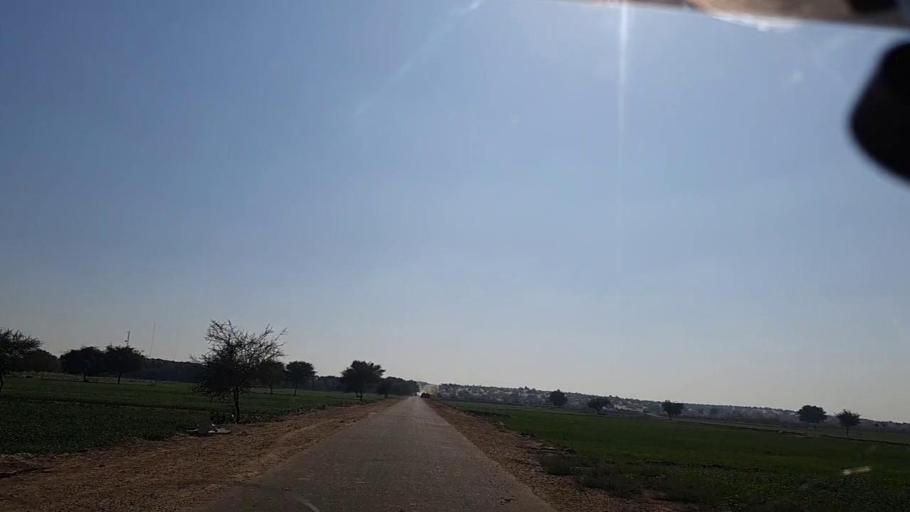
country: PK
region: Sindh
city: Khanpur
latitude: 27.5696
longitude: 69.3888
